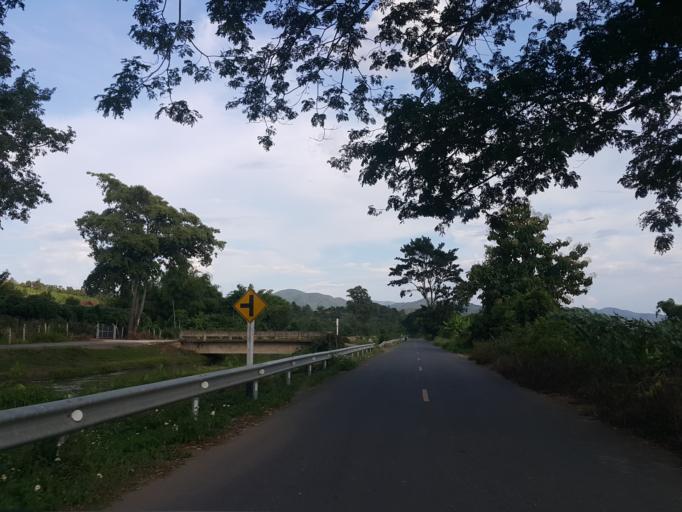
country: TH
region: Chiang Mai
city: Mae Taeng
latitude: 19.0588
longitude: 98.9688
